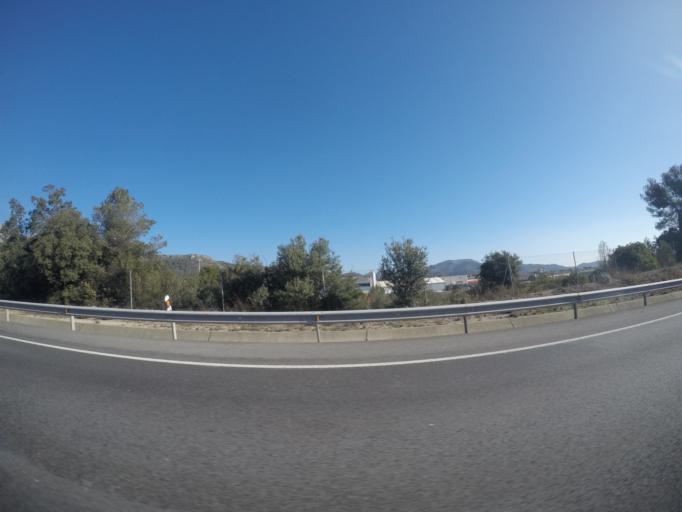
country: ES
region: Catalonia
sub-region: Provincia de Barcelona
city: Esparreguera
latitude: 41.5490
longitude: 1.8487
